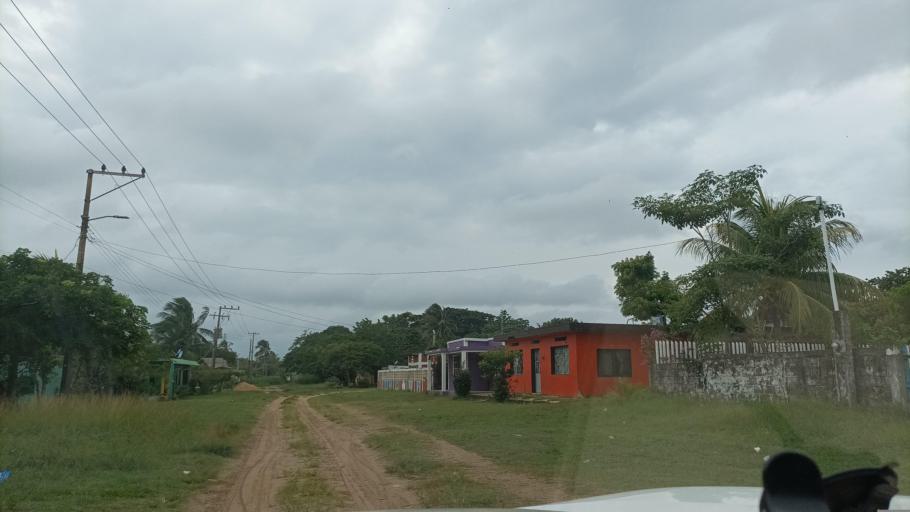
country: MX
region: Veracruz
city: Agua Dulce
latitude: 18.2080
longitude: -94.1382
